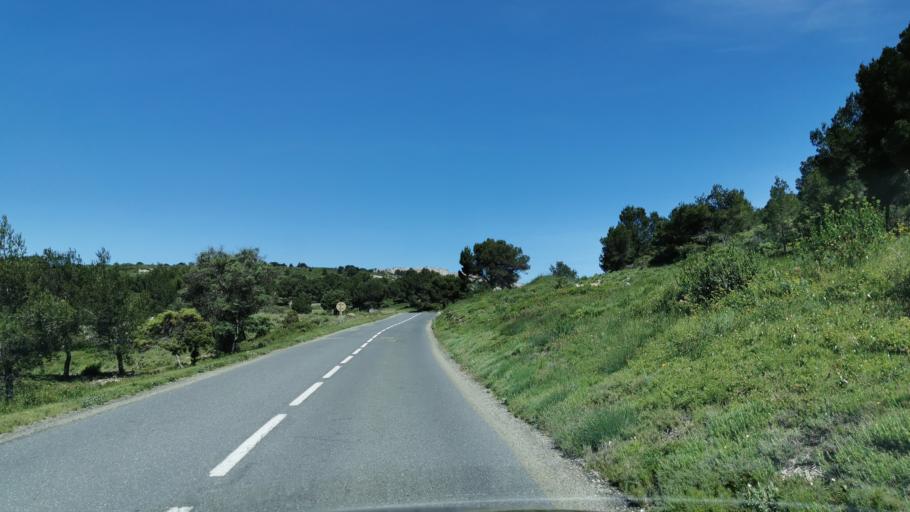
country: FR
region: Languedoc-Roussillon
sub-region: Departement de l'Aude
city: Armissan
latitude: 43.1613
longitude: 3.1455
